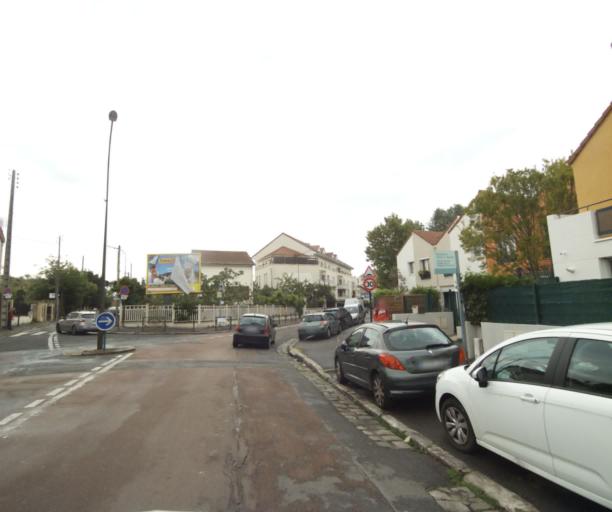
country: FR
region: Ile-de-France
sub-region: Departement du Val-d'Oise
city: Bezons
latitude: 48.9366
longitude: 2.2234
